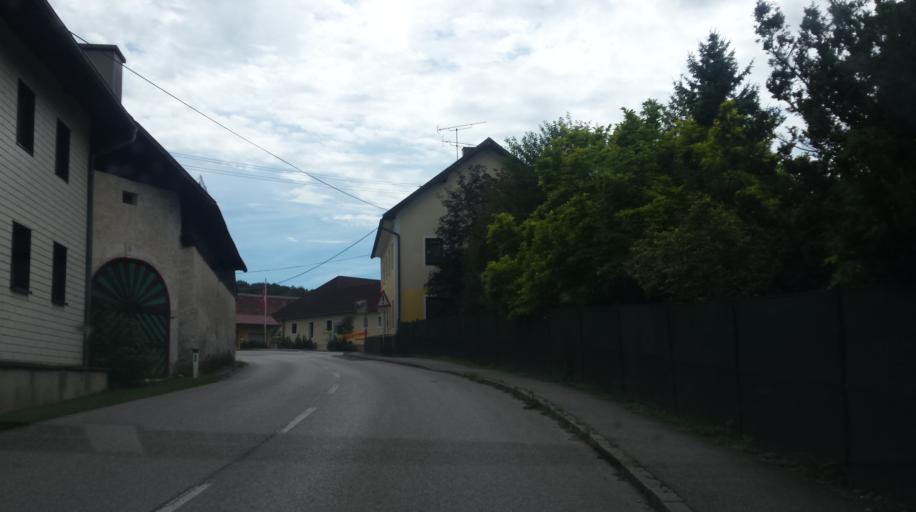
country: AT
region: Upper Austria
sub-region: Wels-Land
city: Bad Wimsbach-Neydharting
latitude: 48.0612
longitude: 13.9014
